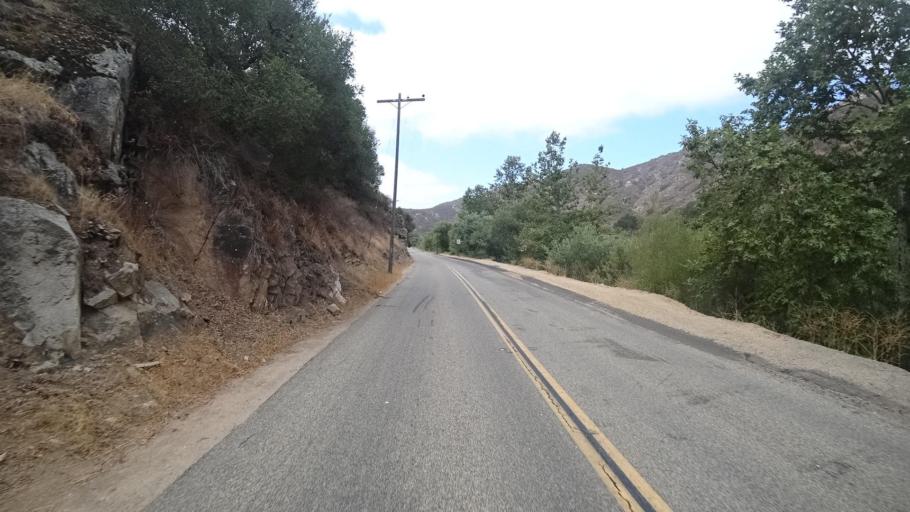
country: US
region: California
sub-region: San Diego County
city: Fallbrook
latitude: 33.4120
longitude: -117.2450
